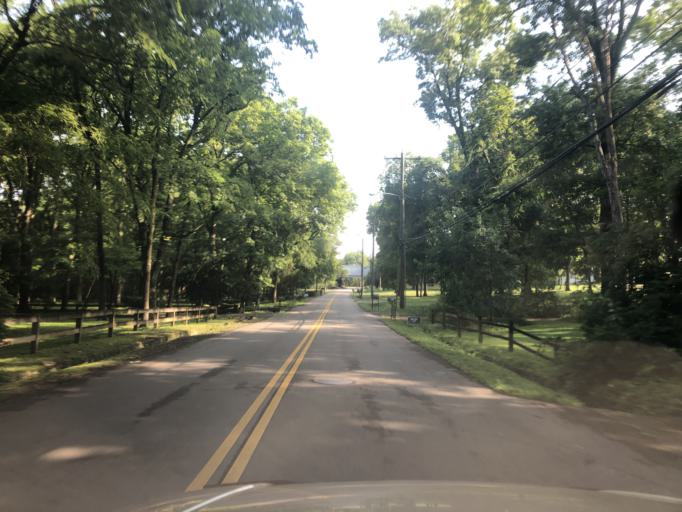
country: US
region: Tennessee
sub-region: Davidson County
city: Lakewood
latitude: 36.2327
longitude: -86.7145
